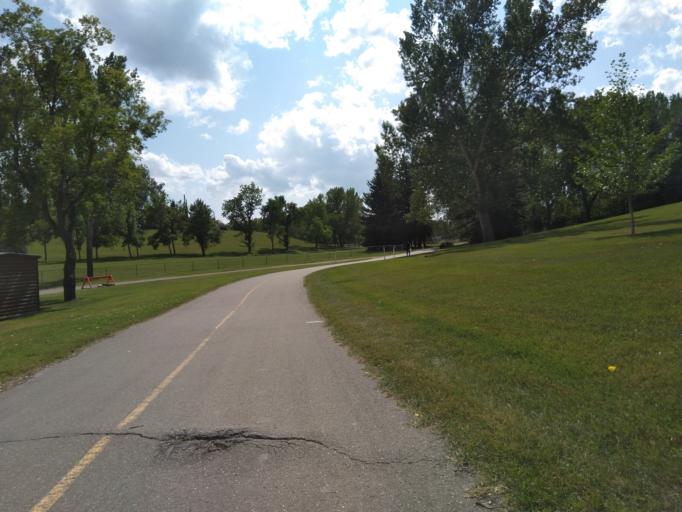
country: CA
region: Alberta
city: Calgary
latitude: 51.0821
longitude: -114.0758
